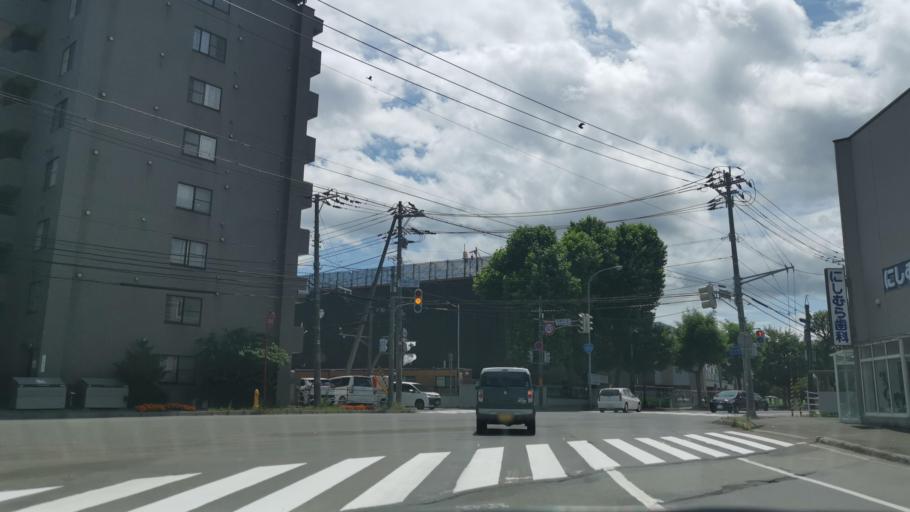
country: JP
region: Hokkaido
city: Sapporo
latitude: 43.0186
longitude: 141.3574
